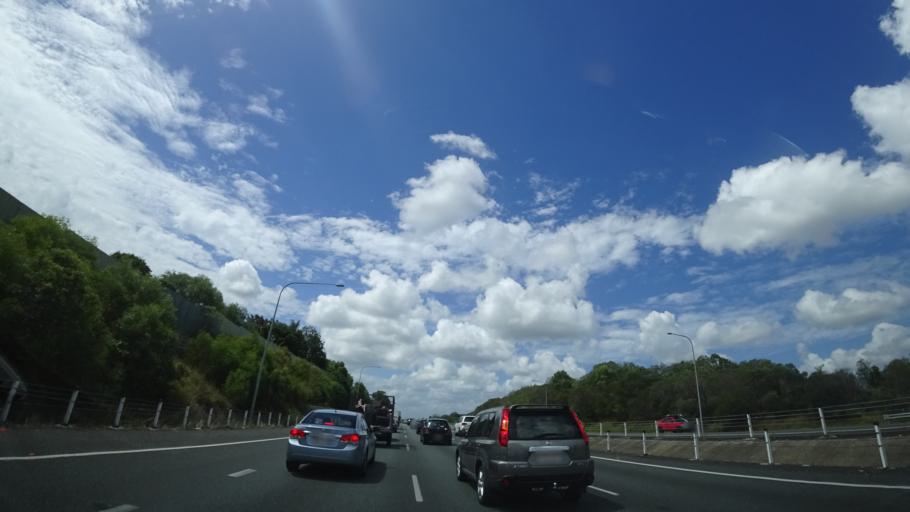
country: AU
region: Queensland
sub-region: Moreton Bay
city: Morayfield
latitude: -27.1027
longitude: 152.9761
